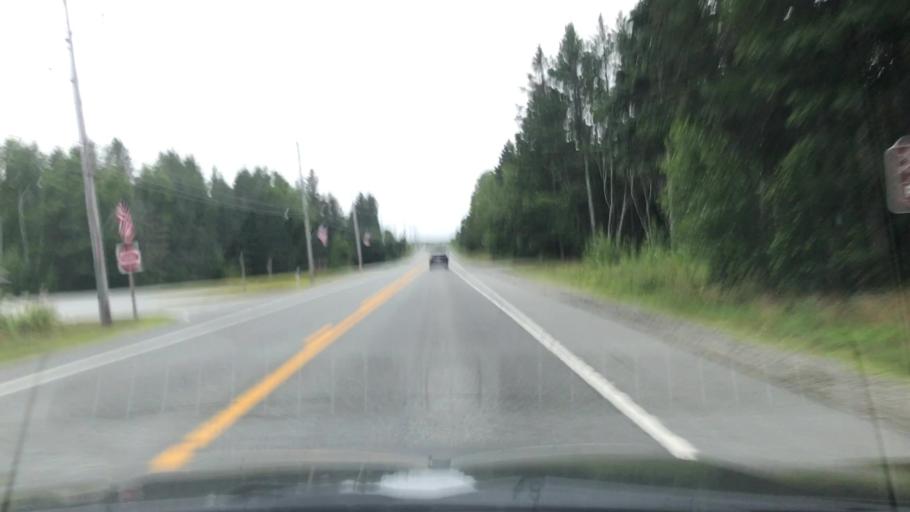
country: US
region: Maine
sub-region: Hancock County
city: Trenton
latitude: 44.4265
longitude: -68.3659
